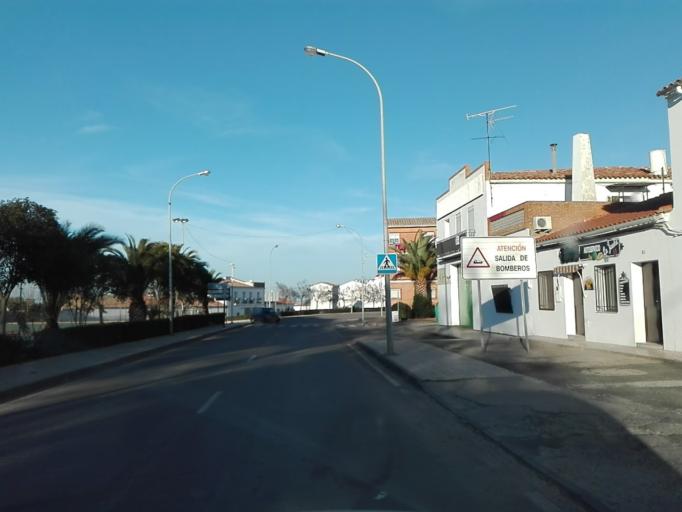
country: ES
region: Extremadura
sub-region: Provincia de Badajoz
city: Llerena
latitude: 38.2395
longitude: -6.0200
